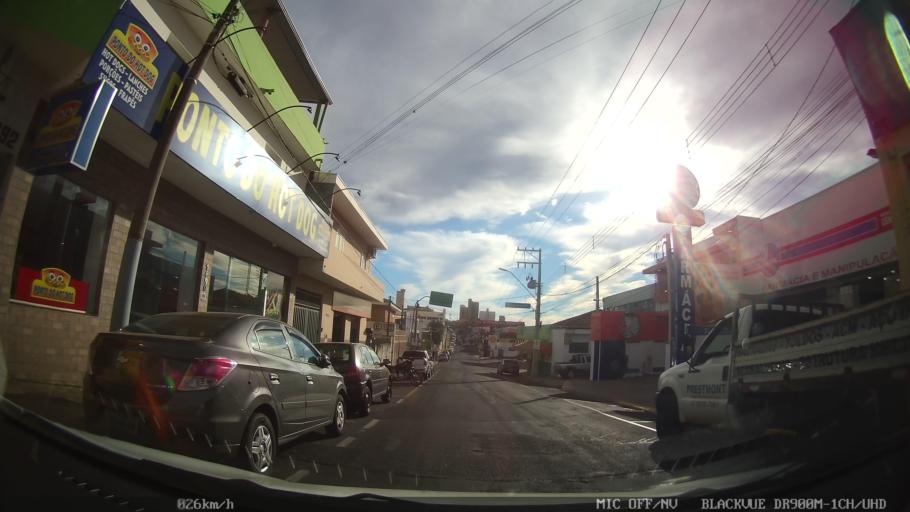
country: BR
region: Sao Paulo
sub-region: Catanduva
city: Catanduva
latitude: -21.1466
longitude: -48.9767
